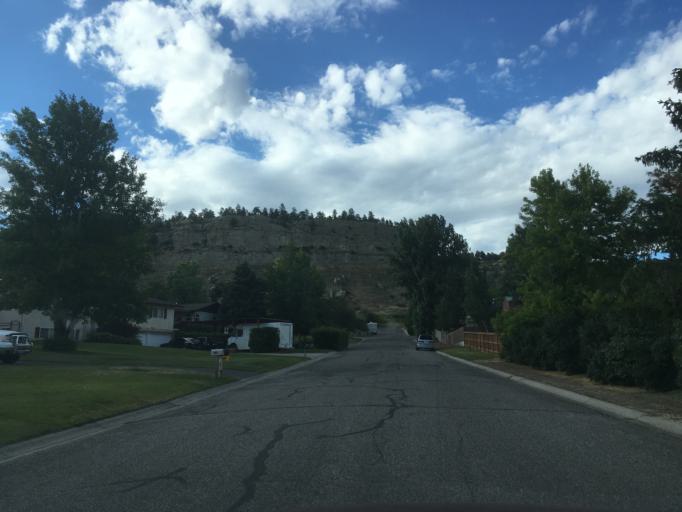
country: US
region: Montana
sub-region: Yellowstone County
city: Billings
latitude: 45.7995
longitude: -108.5958
